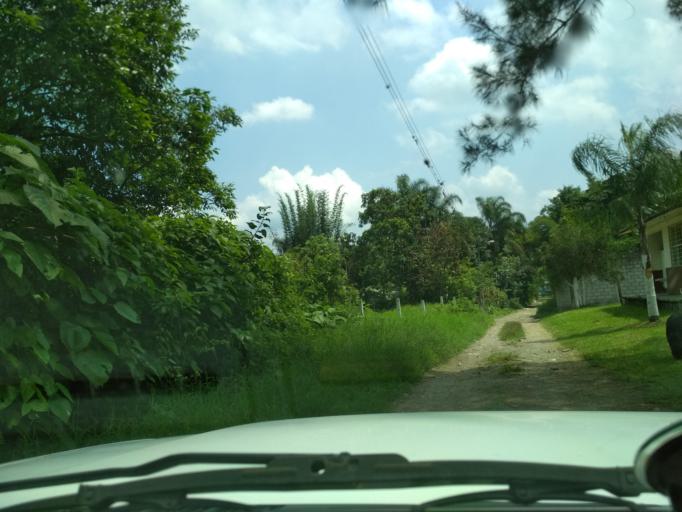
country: MX
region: Veracruz
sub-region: Ixtaczoquitlan
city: Buenavista
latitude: 18.8842
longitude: -97.0480
